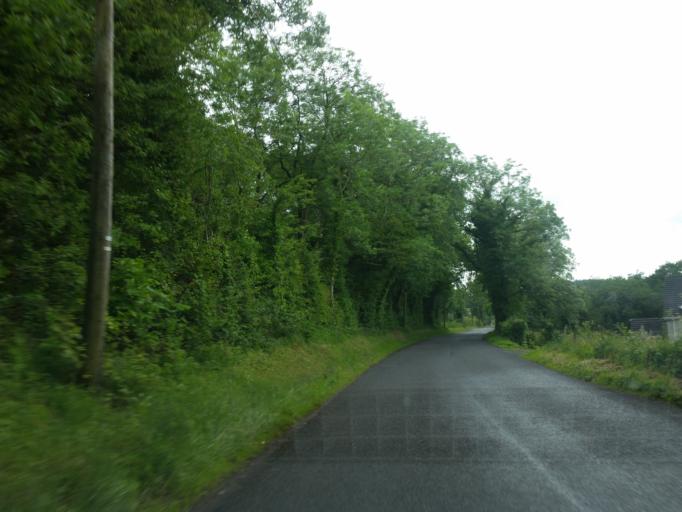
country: GB
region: Northern Ireland
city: Lisnaskea
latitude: 54.2572
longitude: -7.3816
